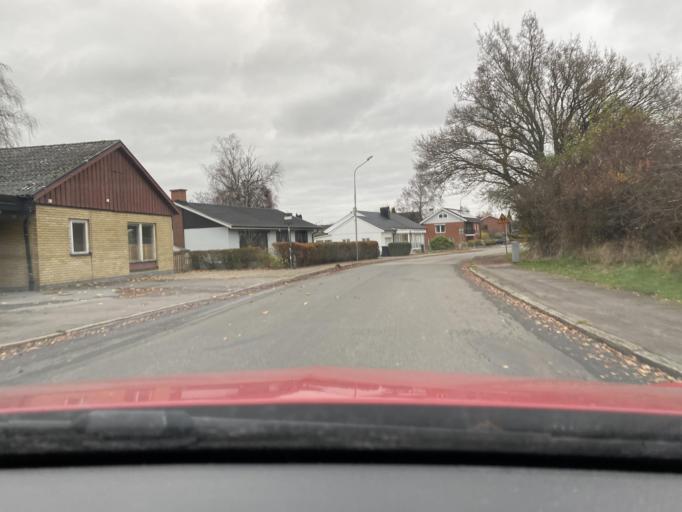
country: SE
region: Skane
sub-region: Hassleholms Kommun
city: Hassleholm
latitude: 56.1593
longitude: 13.7460
